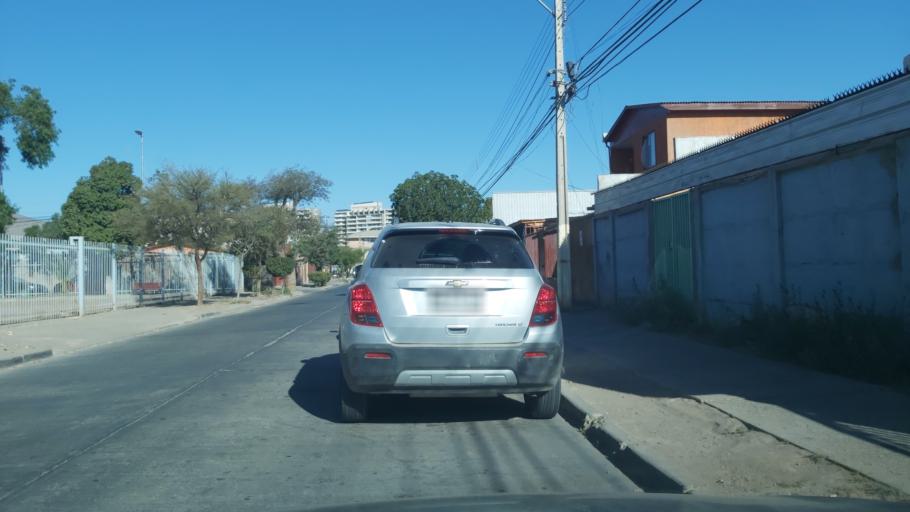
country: CL
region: Atacama
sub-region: Provincia de Copiapo
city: Copiapo
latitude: -27.3755
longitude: -70.3198
